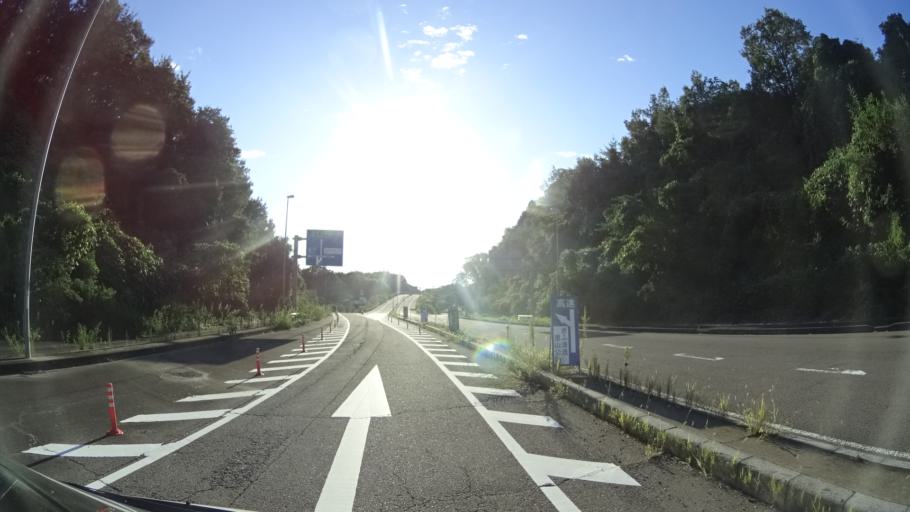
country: JP
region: Gifu
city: Minokamo
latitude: 35.4708
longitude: 137.0307
